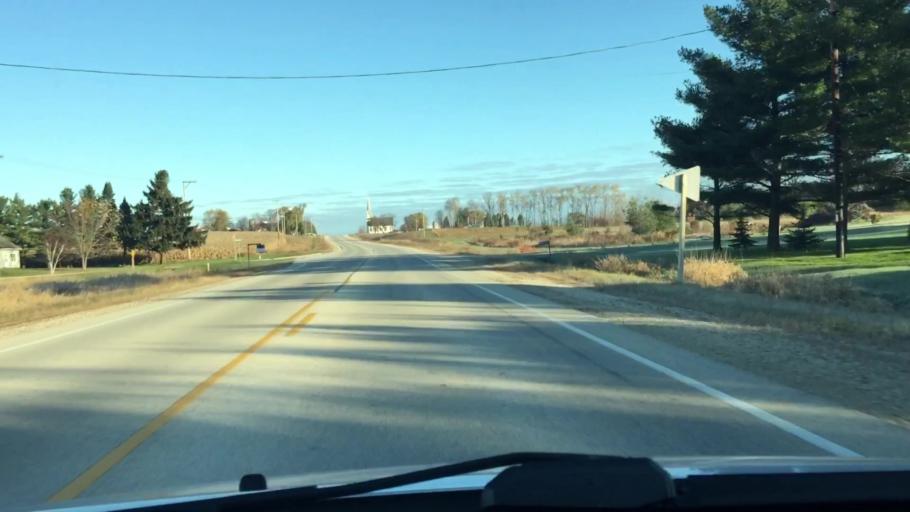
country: US
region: Wisconsin
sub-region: Dodge County
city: Theresa
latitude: 43.5446
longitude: -88.4426
